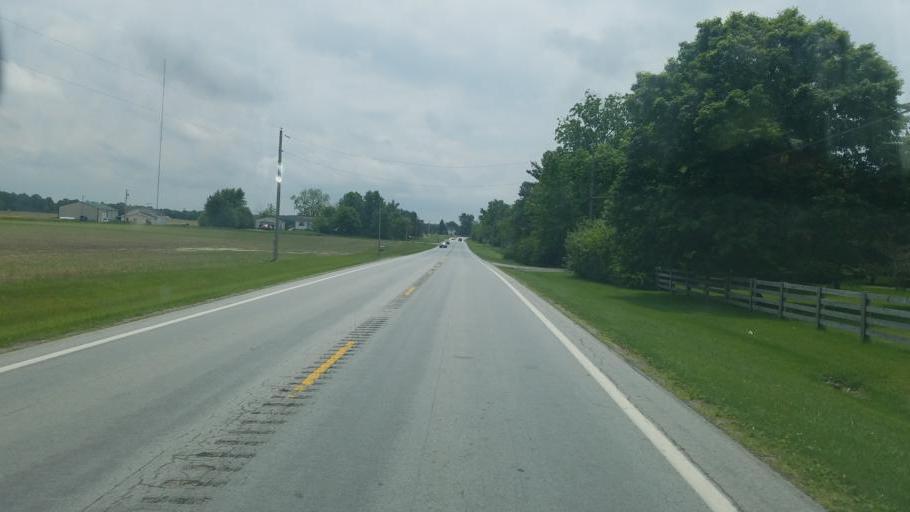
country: US
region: Ohio
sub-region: Union County
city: Marysville
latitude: 40.3138
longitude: -83.3280
